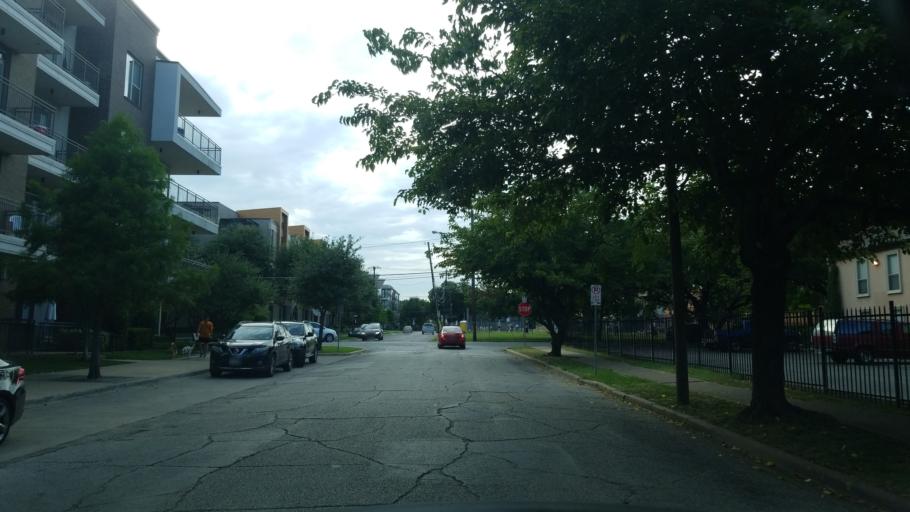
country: US
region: Texas
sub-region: Dallas County
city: Highland Park
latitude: 32.8127
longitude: -96.7798
